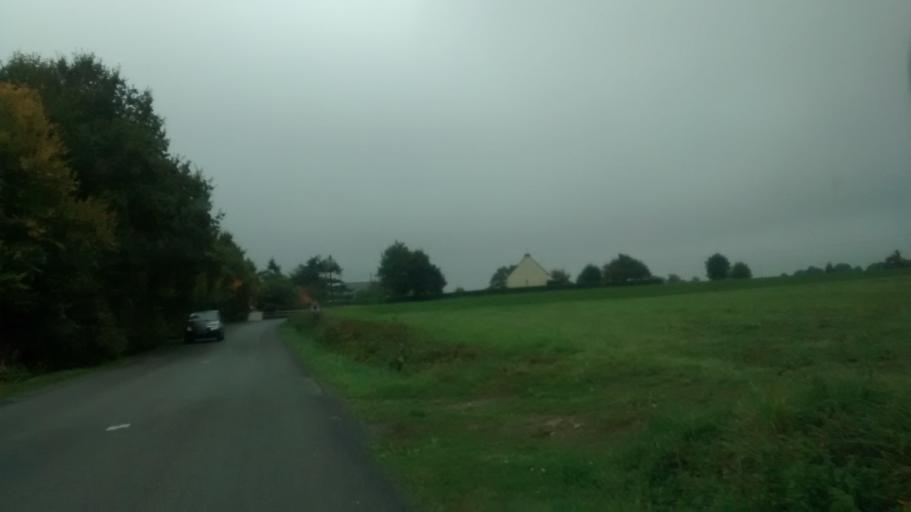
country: FR
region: Brittany
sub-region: Departement d'Ille-et-Vilaine
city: Pace
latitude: 48.1457
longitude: -1.7955
